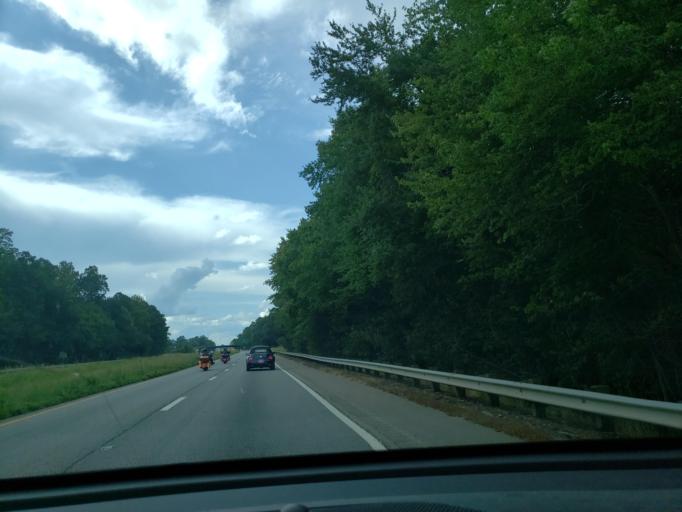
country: US
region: Virginia
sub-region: City of Franklin
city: Franklin
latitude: 36.6443
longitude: -76.9047
